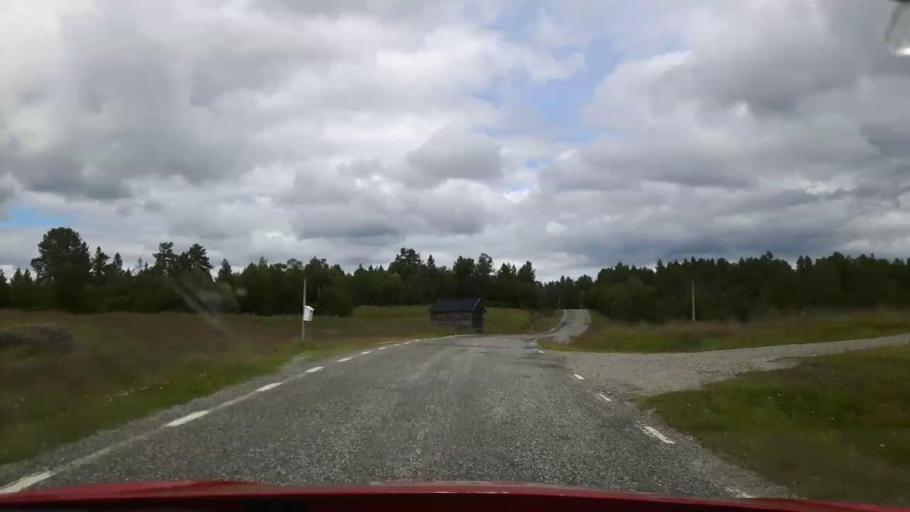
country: NO
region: Hedmark
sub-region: Engerdal
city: Engerdal
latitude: 62.3088
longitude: 12.8074
